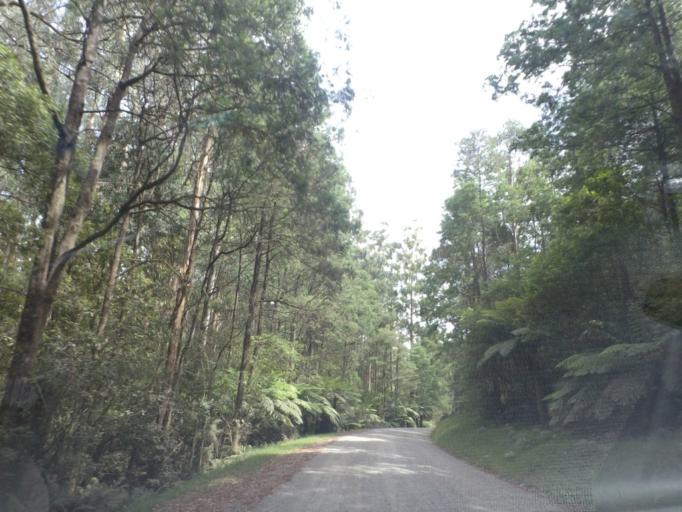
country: AU
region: Victoria
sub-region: Yarra Ranges
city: Healesville
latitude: -37.5495
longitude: 145.5153
